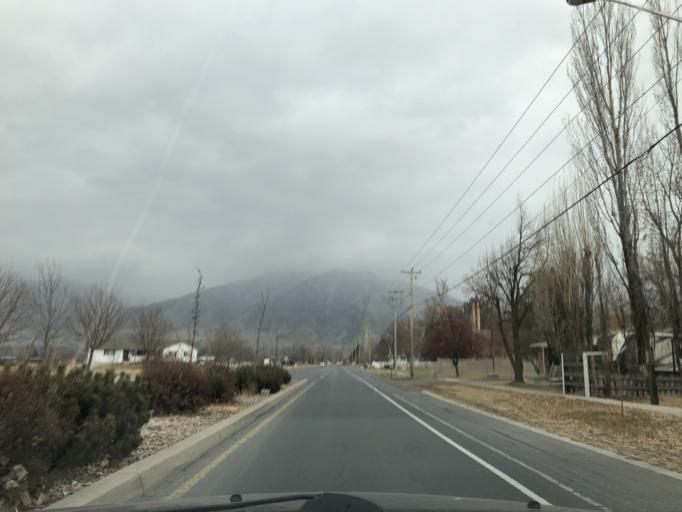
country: US
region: Utah
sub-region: Cache County
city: Nibley
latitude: 41.6748
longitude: -111.8439
